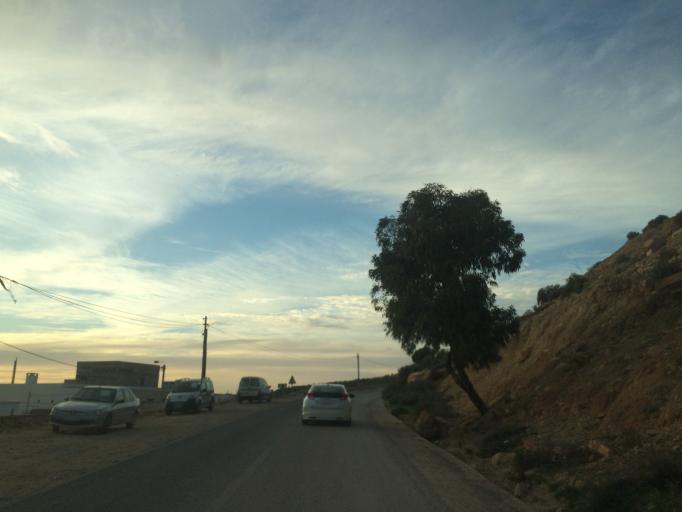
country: MA
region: Souss-Massa-Draa
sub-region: Agadir-Ida-ou-Tnan
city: Taghazout
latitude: 30.5461
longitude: -9.7139
